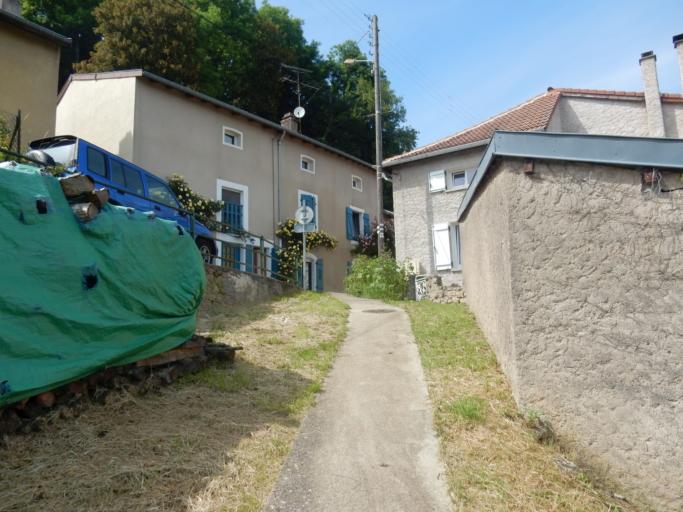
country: FR
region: Lorraine
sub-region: Departement de Meurthe-et-Moselle
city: Pagny-sur-Moselle
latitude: 48.9776
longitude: 5.9959
